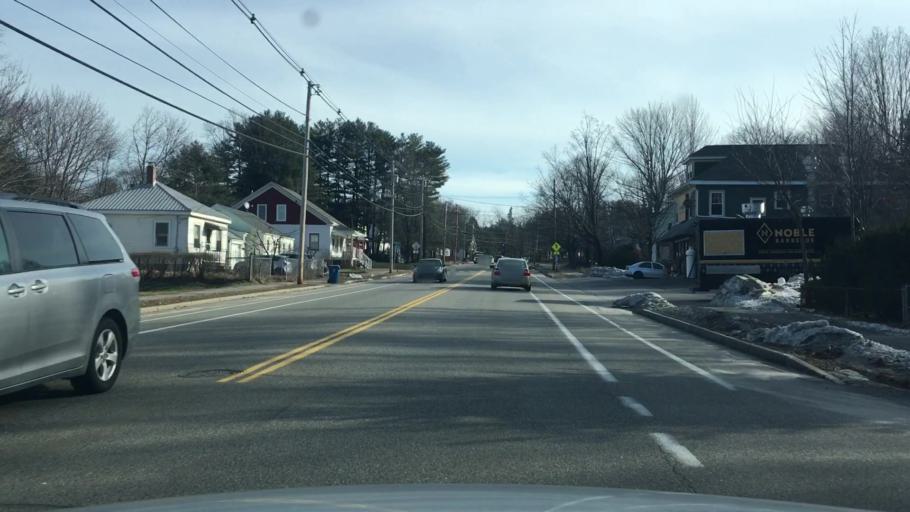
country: US
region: Maine
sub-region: Cumberland County
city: South Portland Gardens
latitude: 43.6990
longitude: -70.3126
